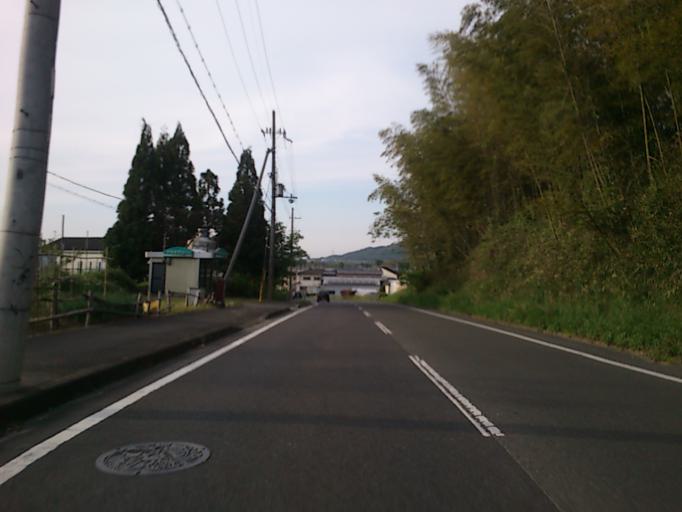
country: JP
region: Kyoto
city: Tanabe
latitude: 34.7683
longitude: 135.8150
